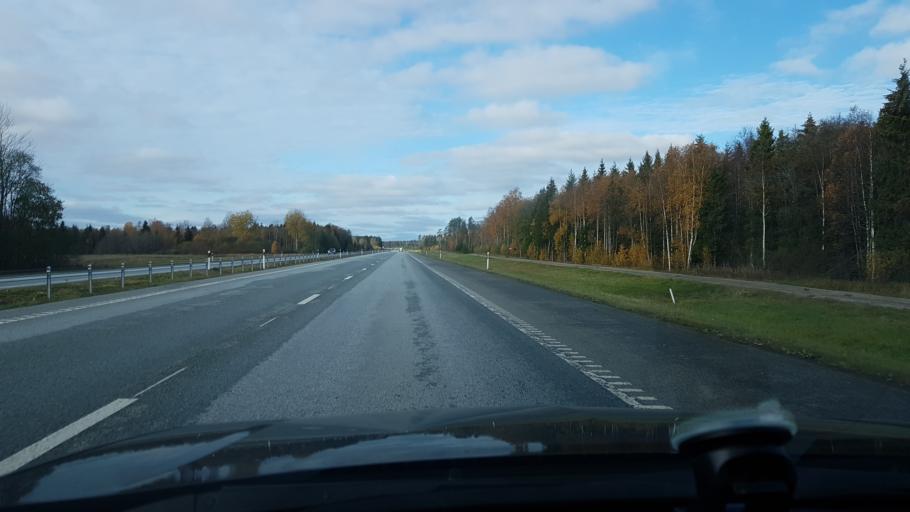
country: EE
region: Laeaene-Virumaa
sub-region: Kadrina vald
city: Kadrina
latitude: 59.4526
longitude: 26.0595
